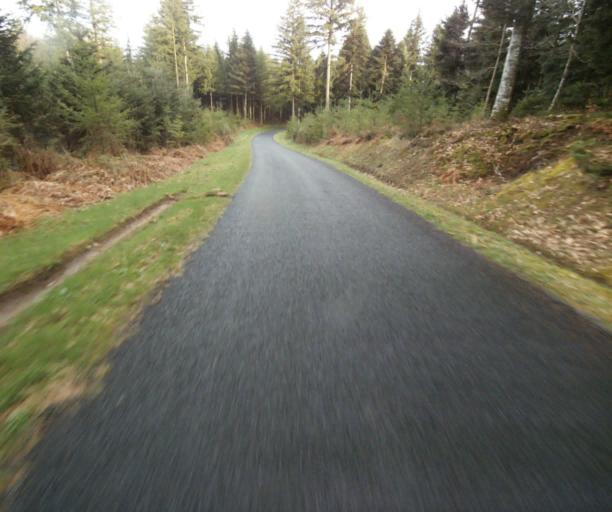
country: FR
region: Limousin
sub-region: Departement de la Correze
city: Argentat
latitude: 45.2129
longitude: 1.9439
